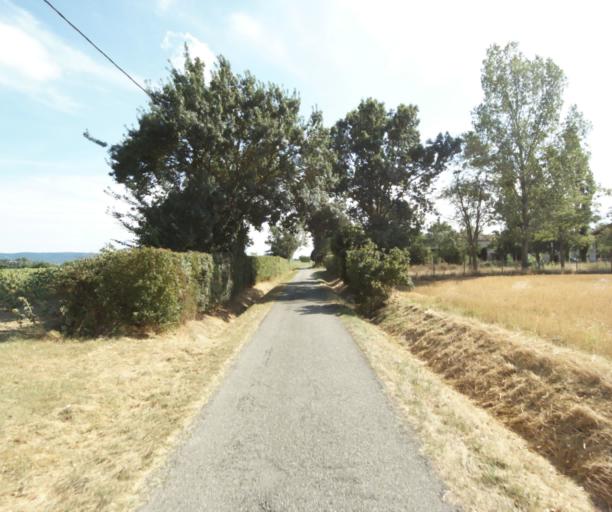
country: FR
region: Midi-Pyrenees
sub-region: Departement de la Haute-Garonne
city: Revel
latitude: 43.5160
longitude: 1.9853
